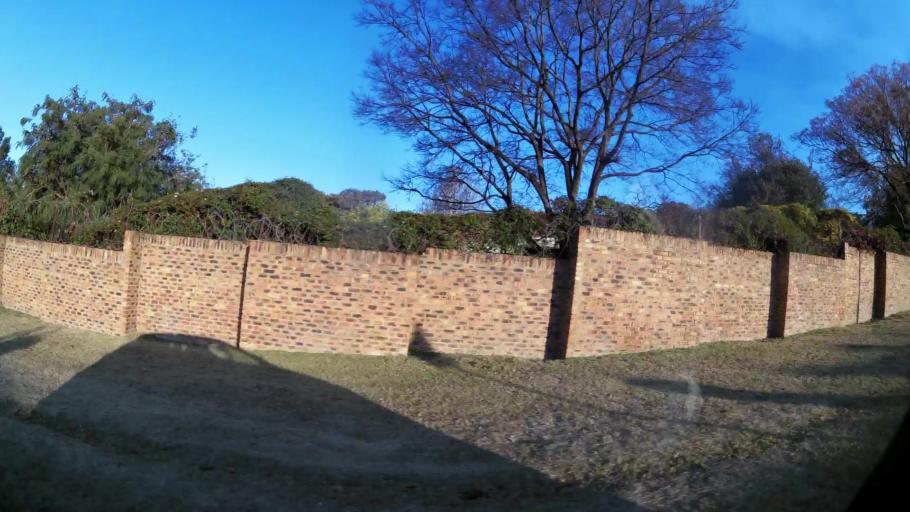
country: ZA
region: Gauteng
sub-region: City of Johannesburg Metropolitan Municipality
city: Diepsloot
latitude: -26.0368
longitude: 27.9781
